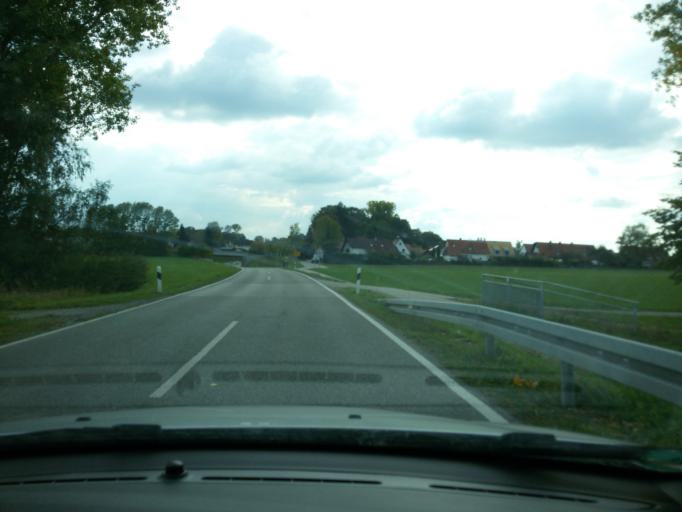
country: DE
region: Bavaria
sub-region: Swabia
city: Buchloe
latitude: 48.0462
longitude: 10.7321
